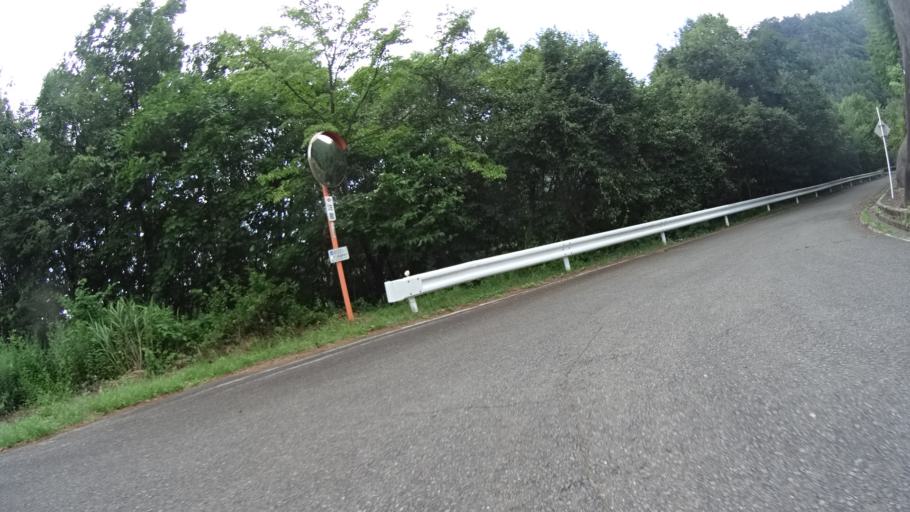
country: JP
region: Nagano
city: Saku
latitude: 36.0679
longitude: 138.6360
